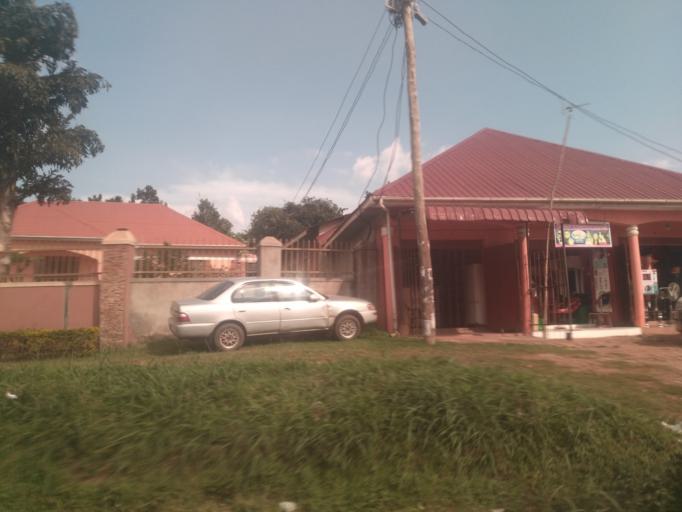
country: UG
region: Central Region
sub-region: Wakiso District
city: Kajansi
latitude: 0.2758
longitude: 32.4681
